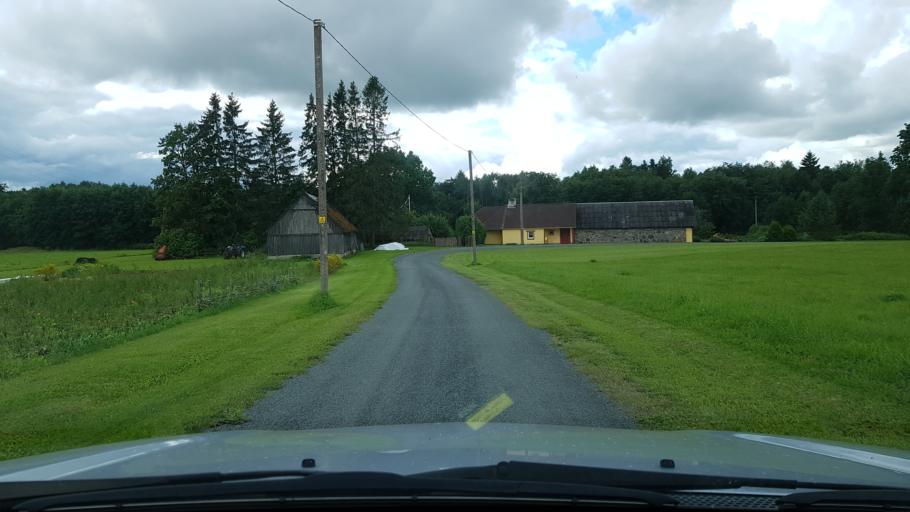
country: EE
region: Harju
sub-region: Raasiku vald
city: Arukula
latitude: 59.2940
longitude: 25.0890
